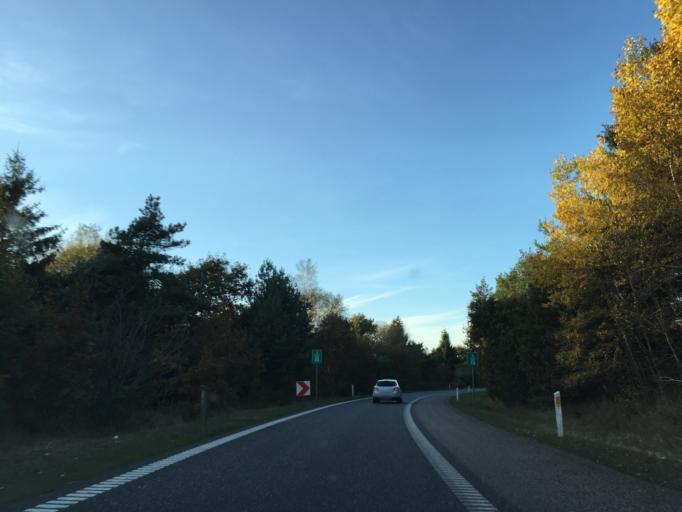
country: DK
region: South Denmark
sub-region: Aabenraa Kommune
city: Krusa
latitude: 54.8747
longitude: 9.3800
